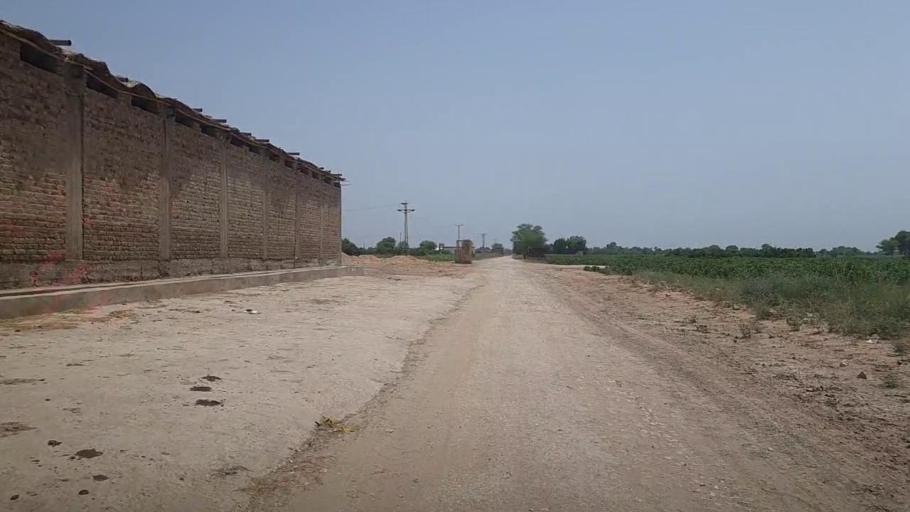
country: PK
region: Sindh
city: Pad Idan
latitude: 26.8424
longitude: 68.3247
